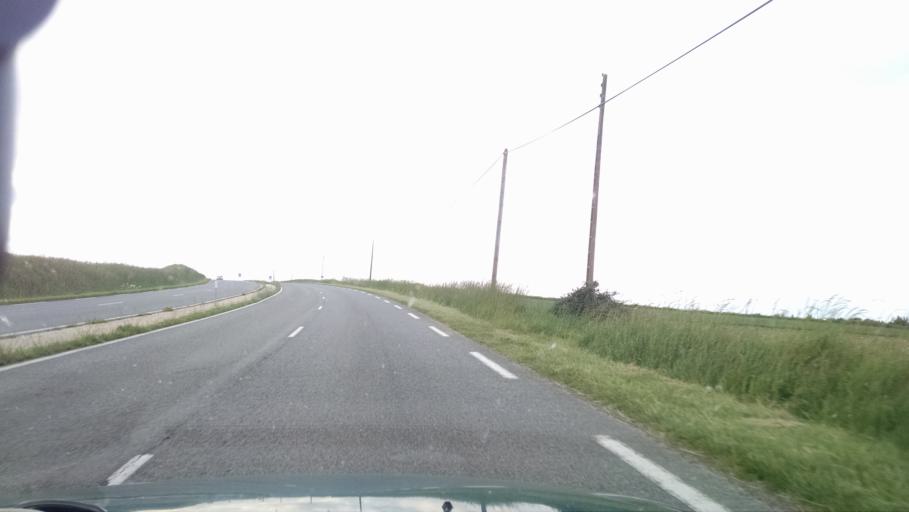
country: FR
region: Brittany
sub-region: Departement du Finistere
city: Saint-Pol-de-Leon
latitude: 48.6536
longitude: -3.9629
